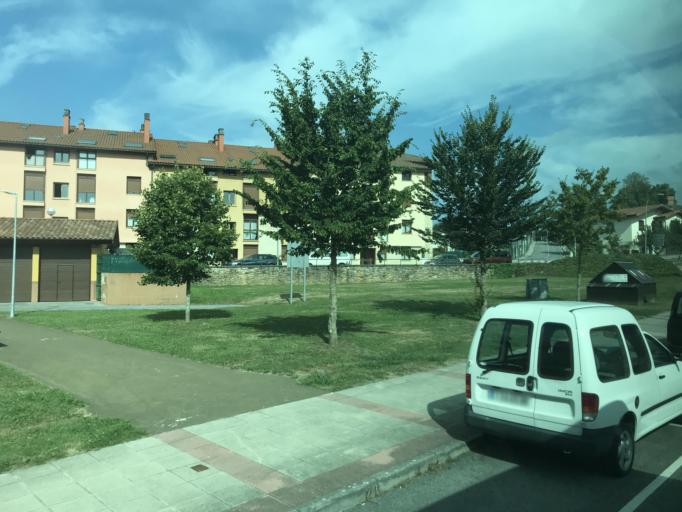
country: ES
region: Basque Country
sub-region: Bizkaia
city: Otxandio
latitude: 43.0429
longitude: -2.6539
